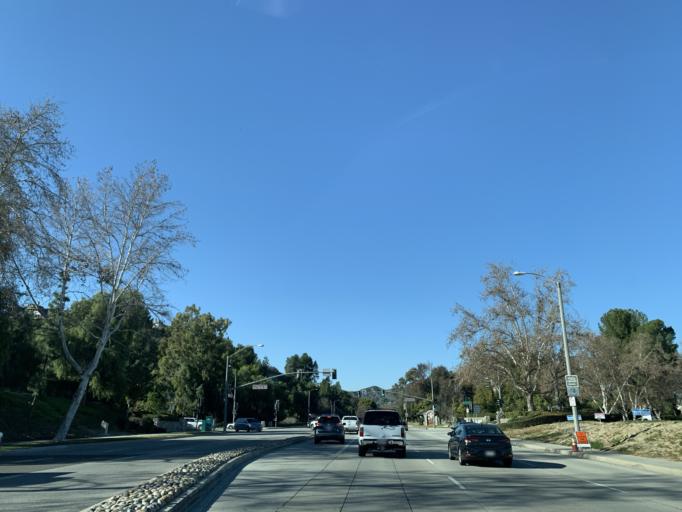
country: US
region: California
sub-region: Los Angeles County
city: Diamond Bar
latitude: 34.0292
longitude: -117.8369
